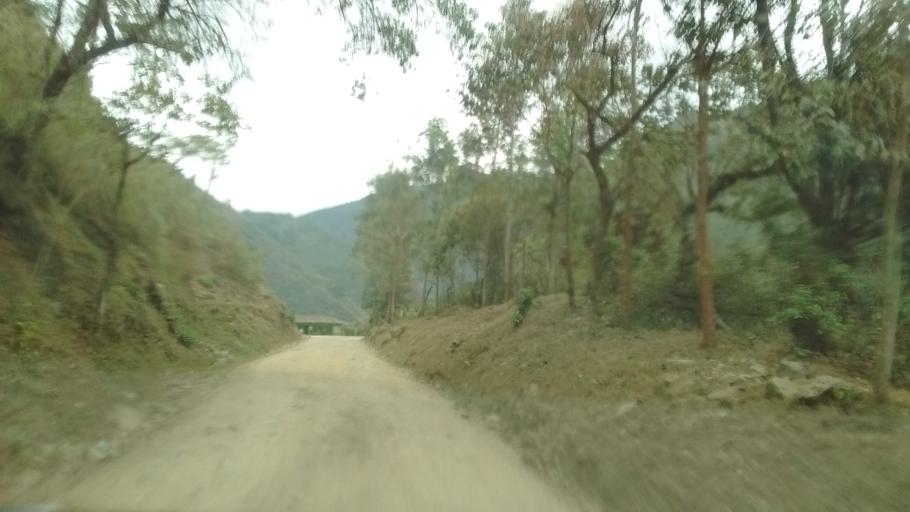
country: CO
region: Cauca
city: La Vega
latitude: 2.0457
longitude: -76.8019
